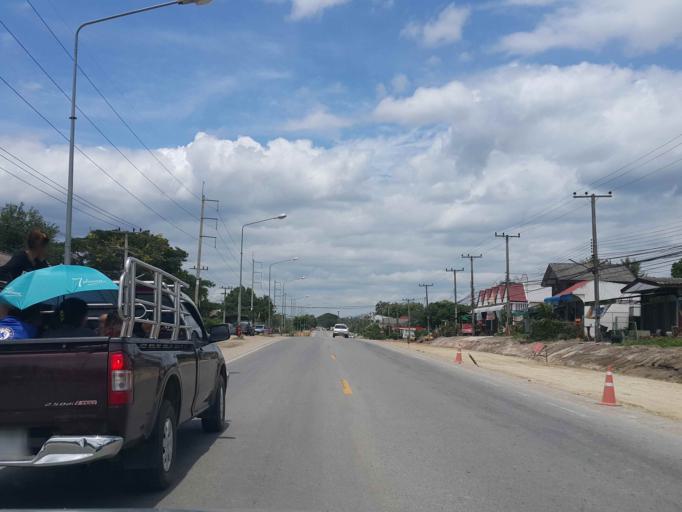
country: TH
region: Lamphun
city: Ban Hong
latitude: 18.3259
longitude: 98.8174
